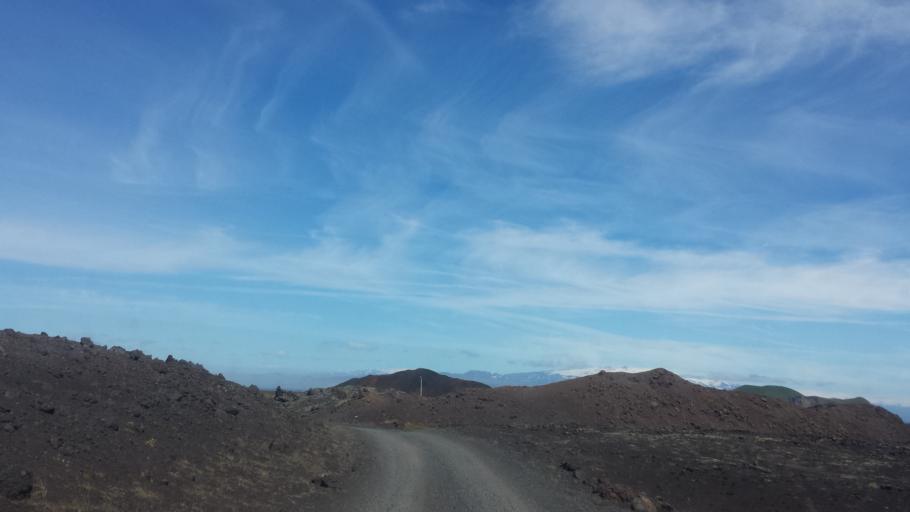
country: IS
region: South
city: Vestmannaeyjar
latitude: 63.4356
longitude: -20.2480
